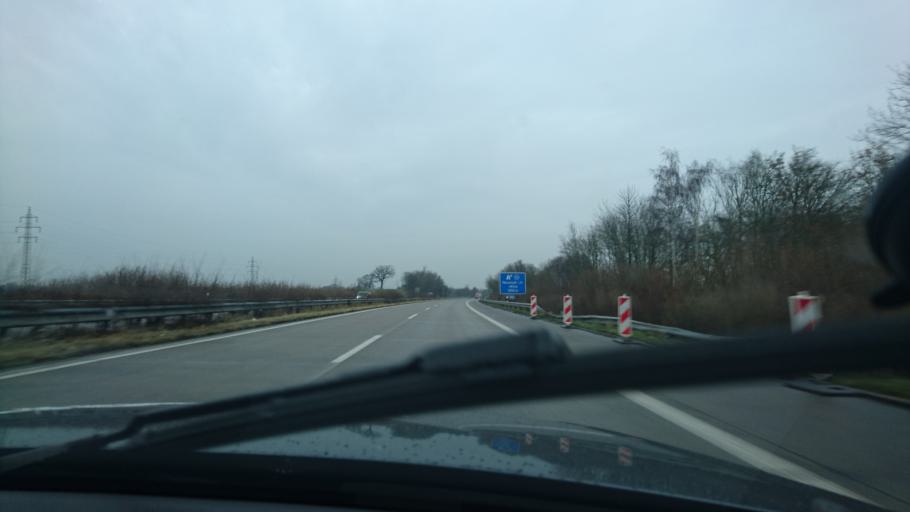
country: DE
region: Schleswig-Holstein
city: Sierksdorf
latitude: 54.0825
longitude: 10.7630
